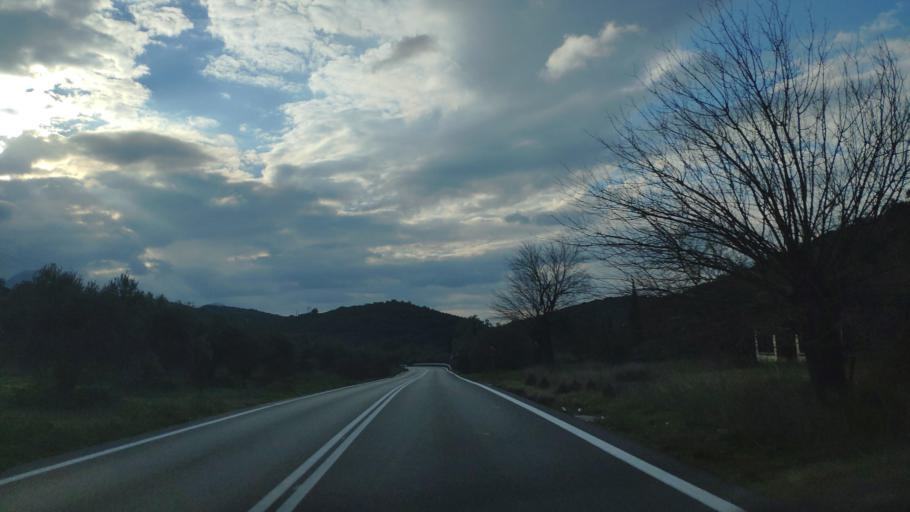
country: GR
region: Peloponnese
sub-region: Nomos Korinthias
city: Ayios Vasilios
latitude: 37.7766
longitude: 22.7247
